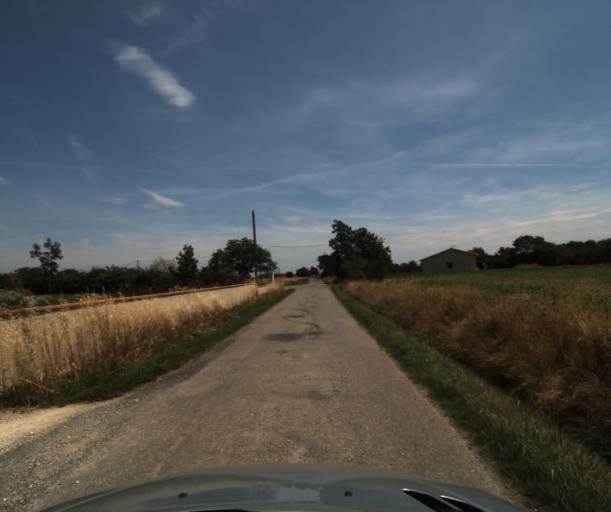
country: FR
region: Midi-Pyrenees
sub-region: Departement de la Haute-Garonne
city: Labastidette
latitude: 43.4619
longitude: 1.2630
